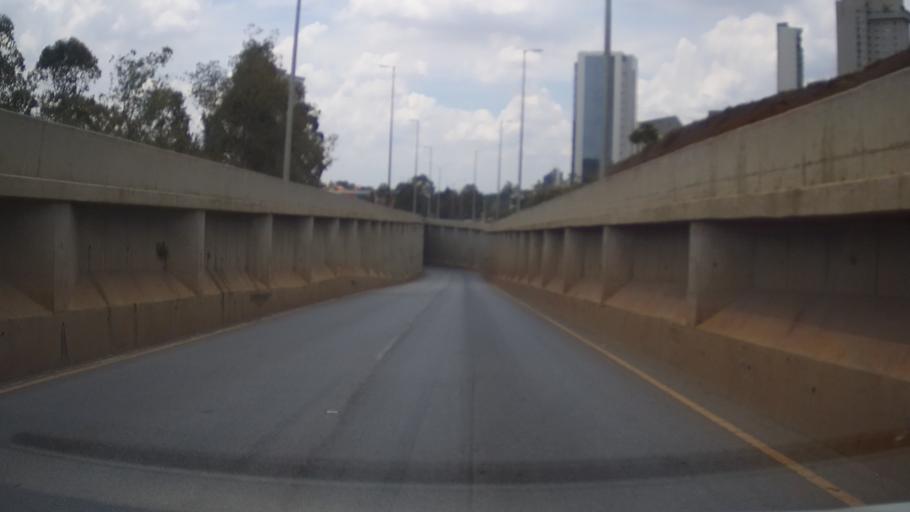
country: BR
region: Minas Gerais
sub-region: Belo Horizonte
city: Belo Horizonte
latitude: -19.9803
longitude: -43.9480
